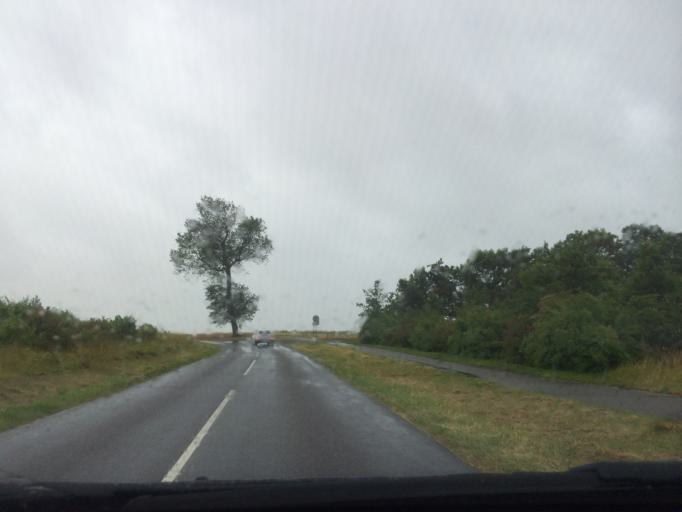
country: DK
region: Zealand
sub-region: Vordingborg Kommune
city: Stege
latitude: 55.0268
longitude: 12.2903
